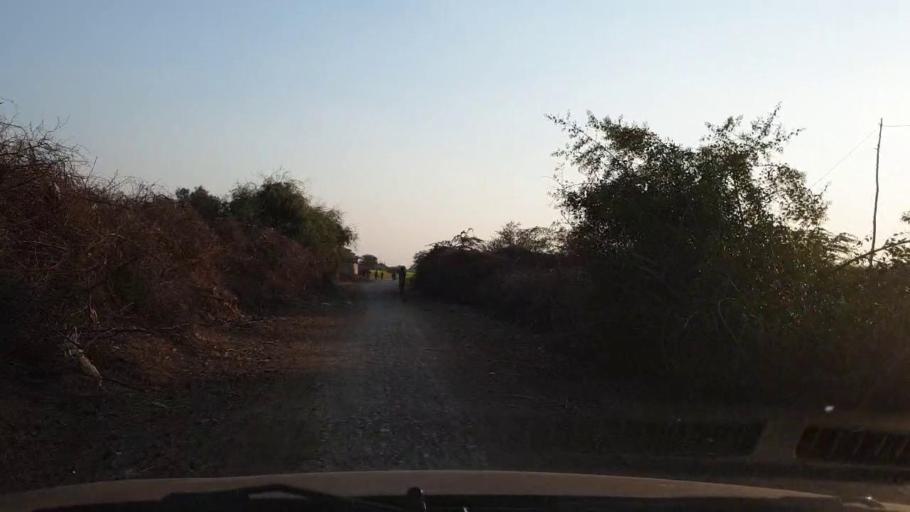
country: PK
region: Sindh
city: Jhol
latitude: 25.9173
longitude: 68.9336
